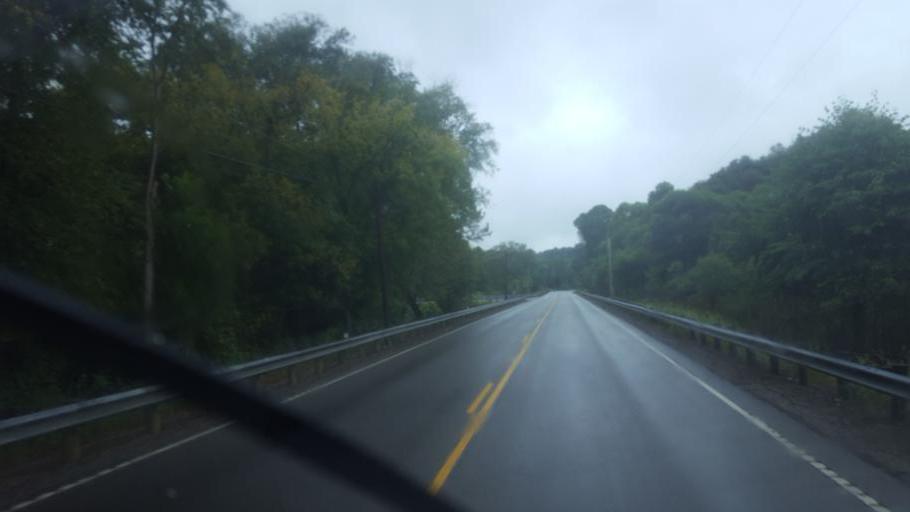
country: US
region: Ohio
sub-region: Jackson County
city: Oak Hill
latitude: 38.8038
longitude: -82.6974
